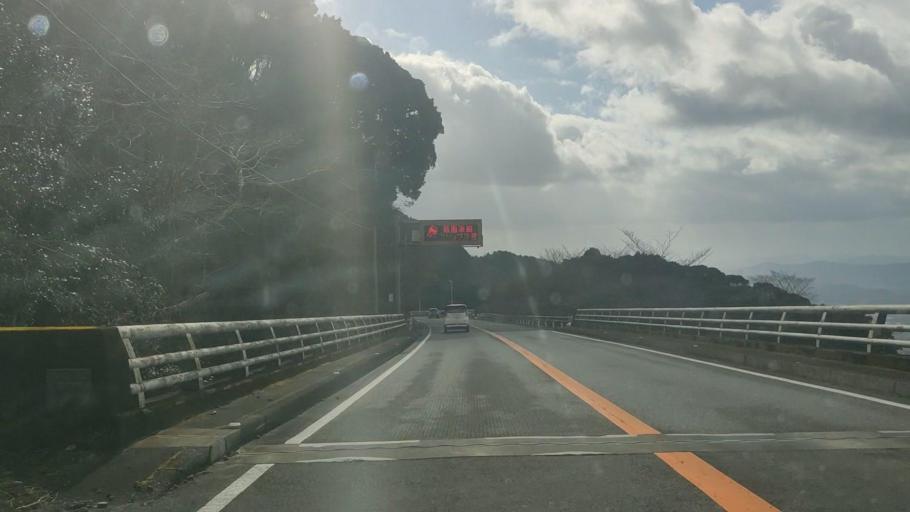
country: JP
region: Kumamoto
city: Hitoyoshi
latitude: 32.0865
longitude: 130.8012
